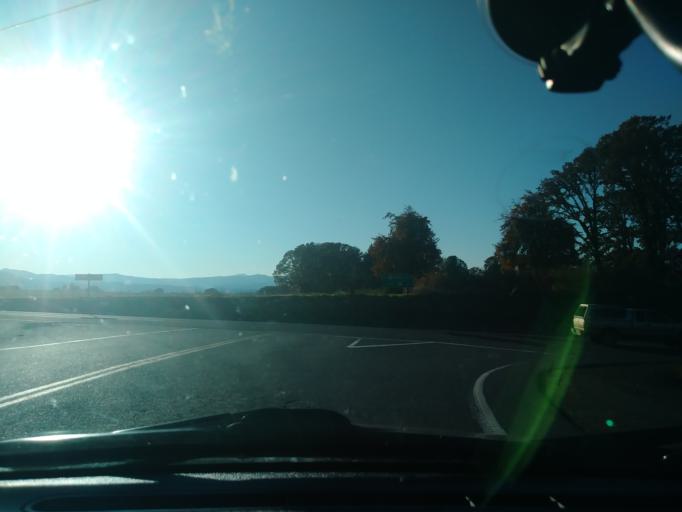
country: US
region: Oregon
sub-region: Washington County
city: Banks
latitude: 45.6078
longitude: -123.1141
